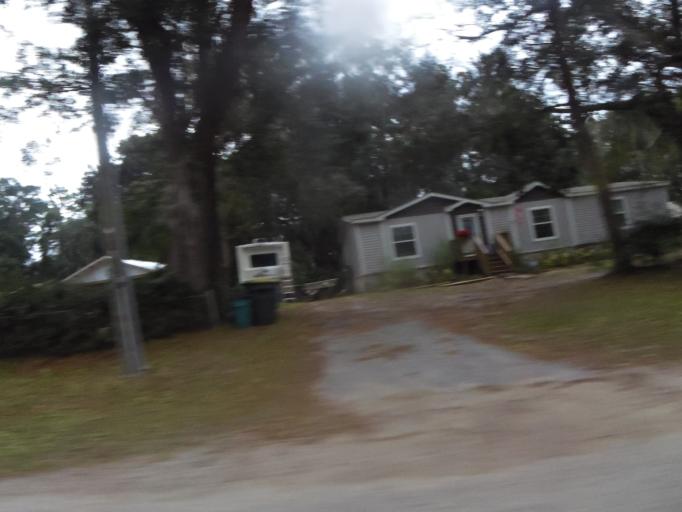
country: US
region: Florida
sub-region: Duval County
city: Jacksonville
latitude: 30.2628
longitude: -81.5817
